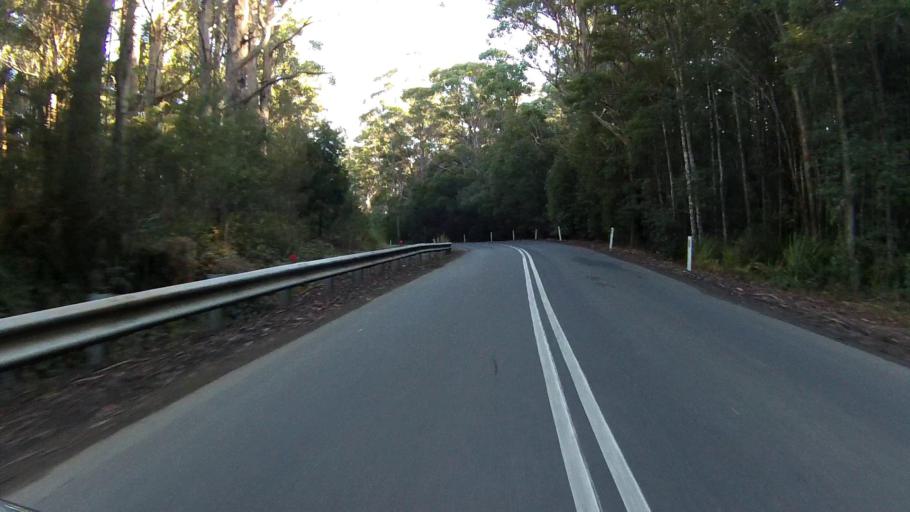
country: AU
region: Tasmania
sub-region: Clarence
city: Sandford
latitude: -43.0978
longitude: 147.8695
